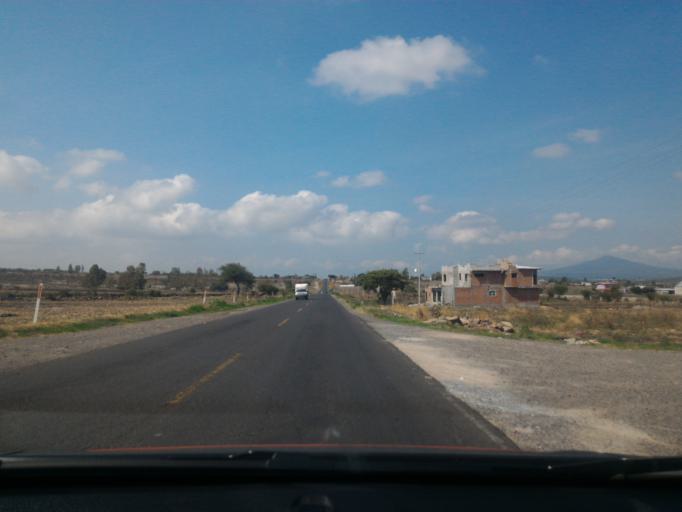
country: MX
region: Guanajuato
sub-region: Penjamo
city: Estacion la Piedad
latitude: 20.4189
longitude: -101.9945
